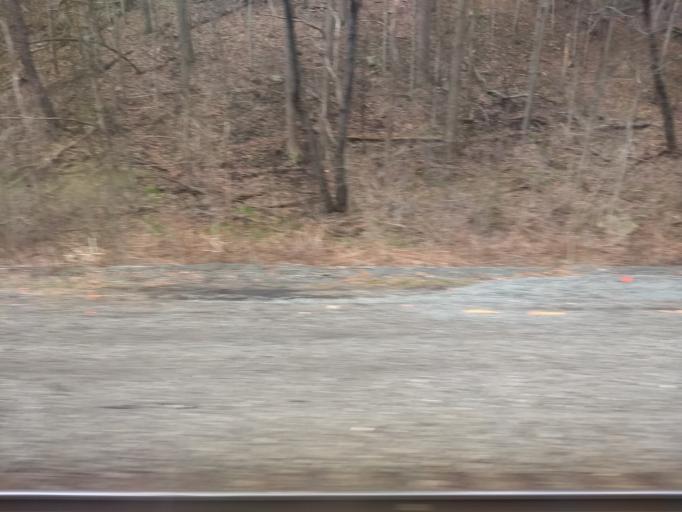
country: US
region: Pennsylvania
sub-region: Huntingdon County
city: McConnellstown
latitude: 40.5932
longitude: -78.1130
